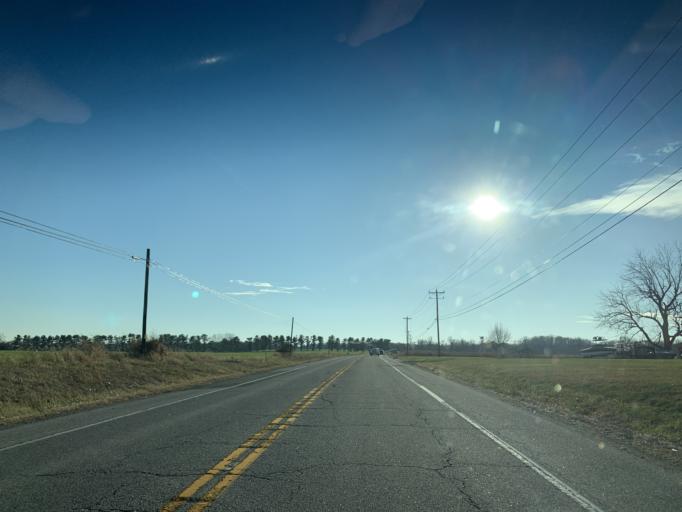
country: US
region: Delaware
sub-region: New Castle County
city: Middletown
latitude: 39.3850
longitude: -75.8741
